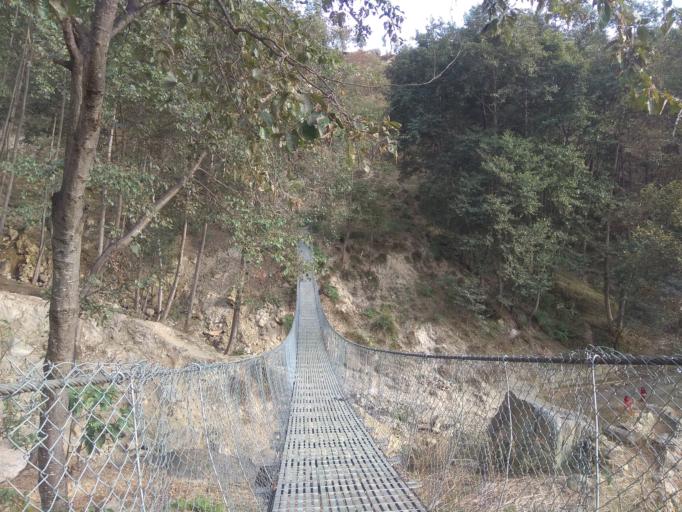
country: NP
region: Far Western
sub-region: Seti Zone
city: Achham
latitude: 29.2542
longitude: 81.6394
